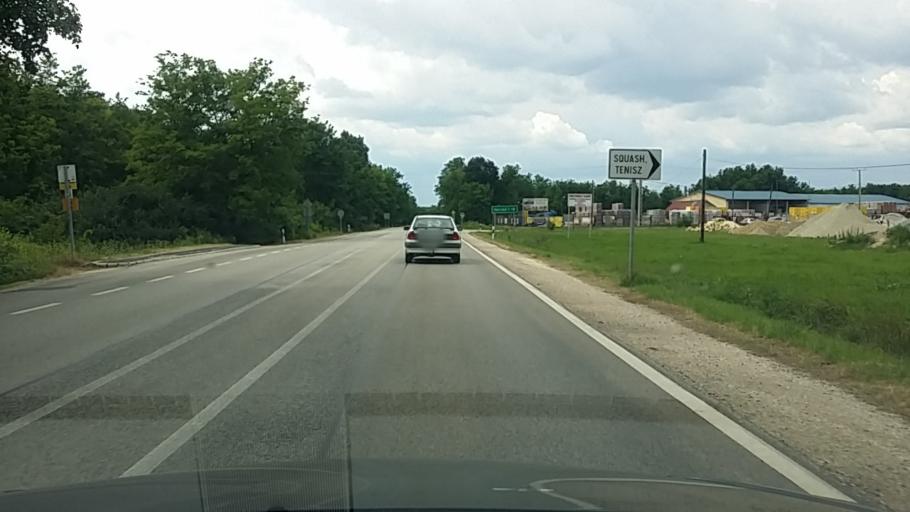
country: HU
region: Pest
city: Hernad
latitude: 47.1507
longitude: 19.3903
